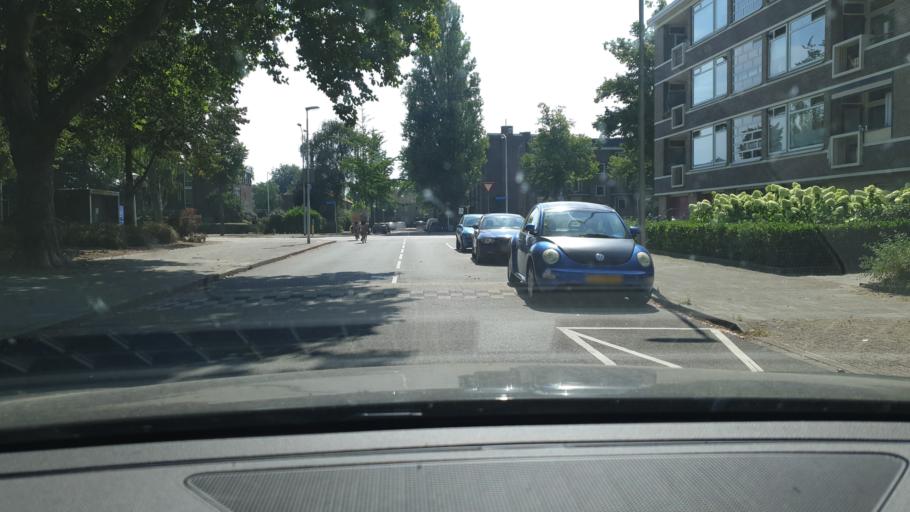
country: NL
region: North Brabant
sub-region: Gemeente Eindhoven
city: Eindhoven
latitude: 51.4329
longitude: 5.4645
